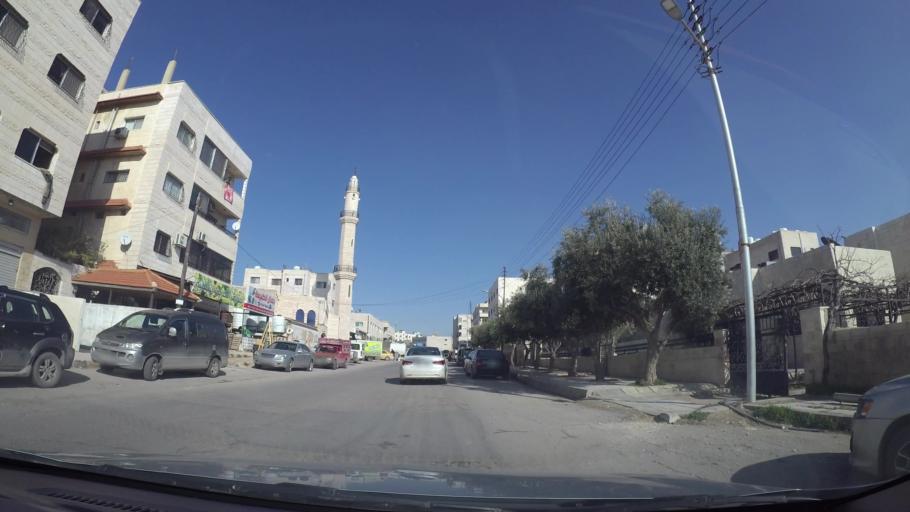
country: JO
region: Amman
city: Al Bunayyat ash Shamaliyah
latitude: 31.9028
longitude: 35.9141
